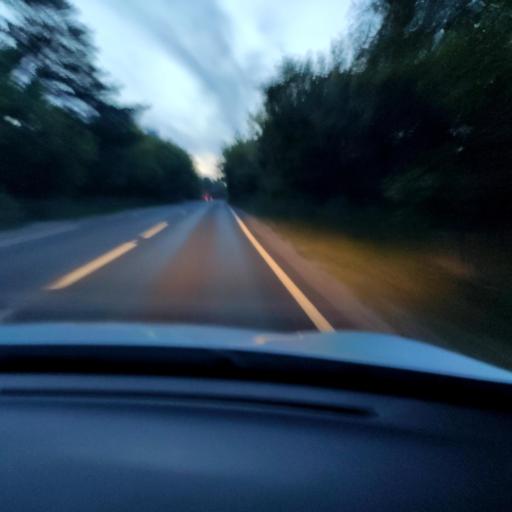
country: RU
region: Tatarstan
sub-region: Gorod Kazan'
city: Kazan
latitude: 55.8981
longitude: 49.0830
